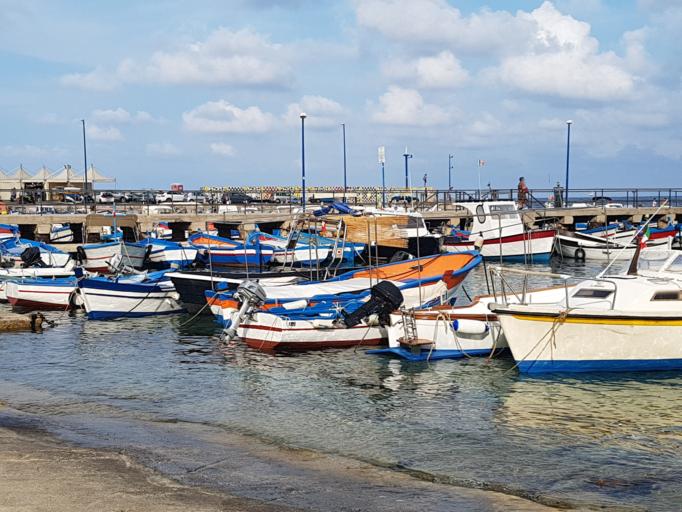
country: IT
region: Sicily
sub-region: Palermo
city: Palermo
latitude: 38.2072
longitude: 13.3264
